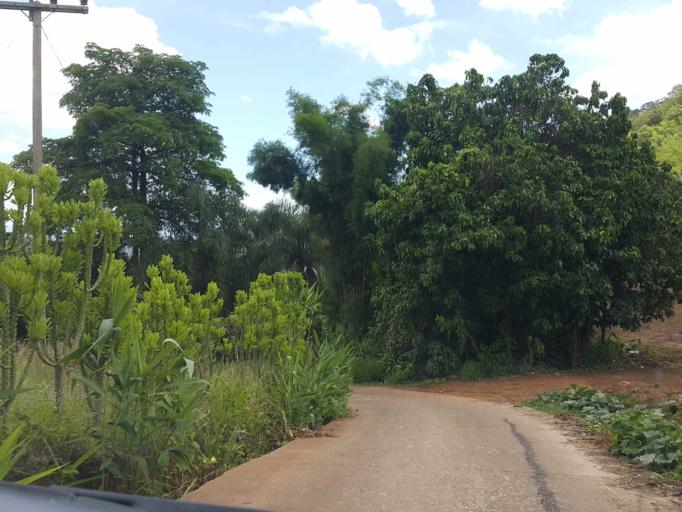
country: TH
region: Chiang Mai
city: Hang Dong
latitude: 18.7770
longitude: 98.8394
